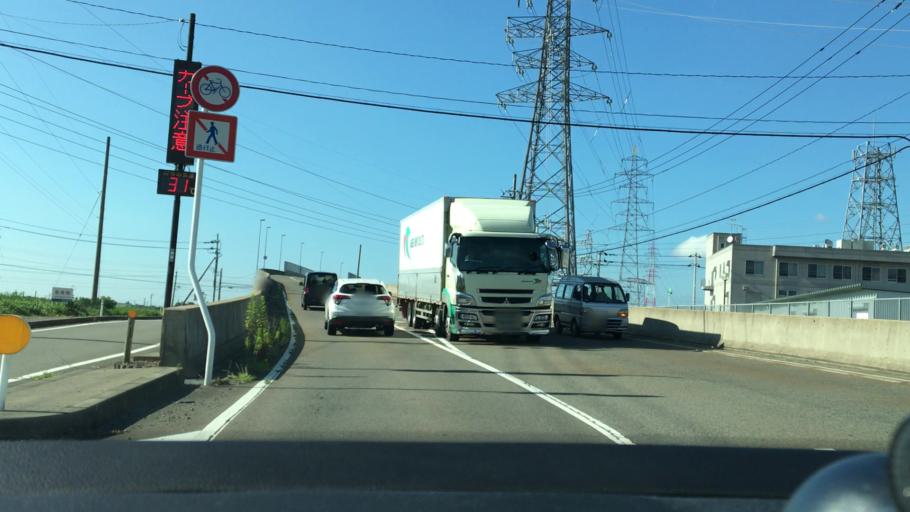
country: JP
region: Fukui
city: Maruoka
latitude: 36.0904
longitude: 136.2822
